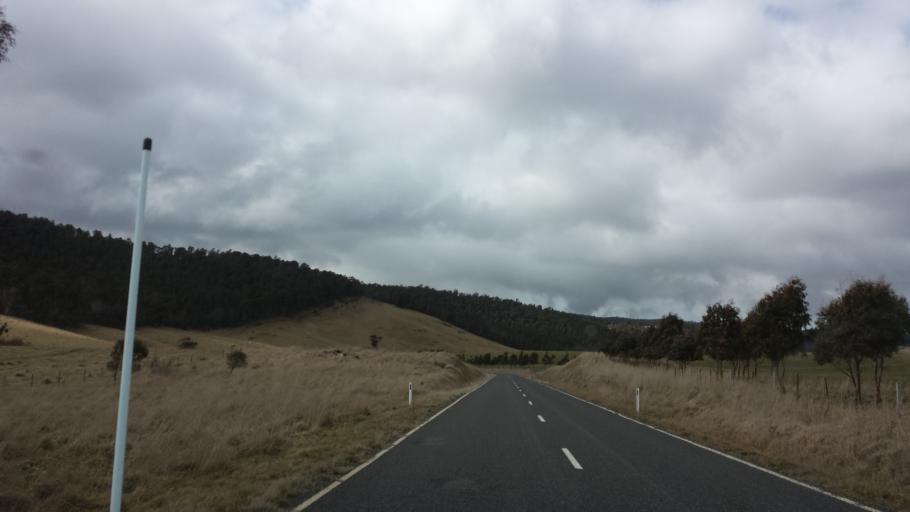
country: AU
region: Victoria
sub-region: Alpine
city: Mount Beauty
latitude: -37.1333
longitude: 147.4727
